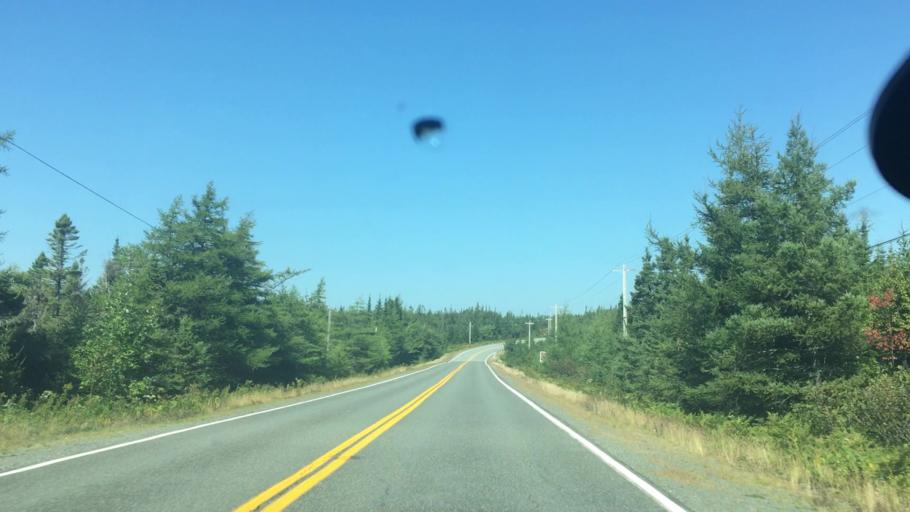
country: CA
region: Nova Scotia
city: Antigonish
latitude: 45.0061
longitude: -62.1042
